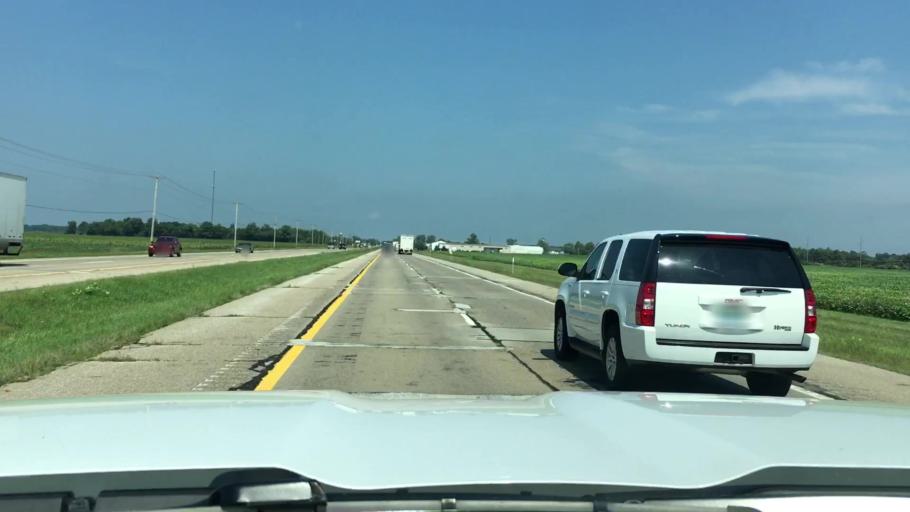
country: US
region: Michigan
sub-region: Kalamazoo County
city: Schoolcraft
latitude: 42.0828
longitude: -85.6366
